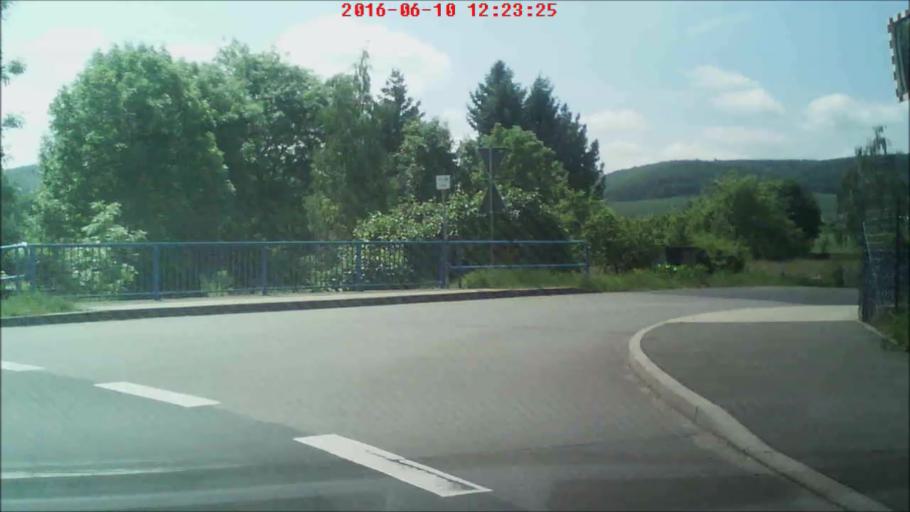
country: DE
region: Thuringia
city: Obermassfeld-Grimmenthal
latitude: 50.5266
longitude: 10.4378
